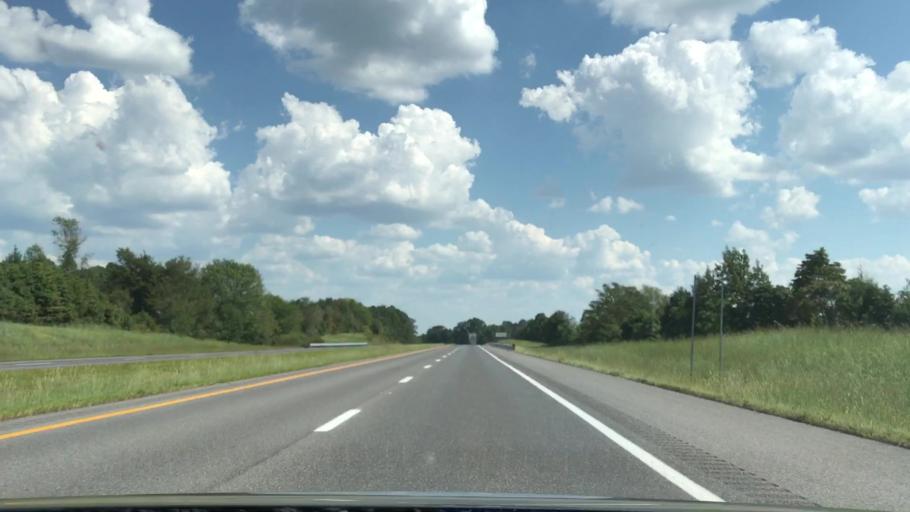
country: US
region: Kentucky
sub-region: Lyon County
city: Eddyville
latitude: 37.1075
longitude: -87.9942
